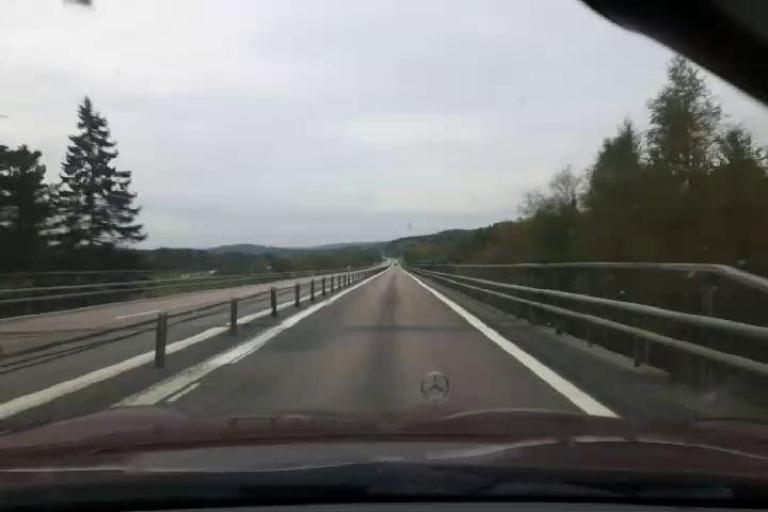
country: SE
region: Vaesternorrland
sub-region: Haernoesands Kommun
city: Haernoesand
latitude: 62.8578
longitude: 18.0213
